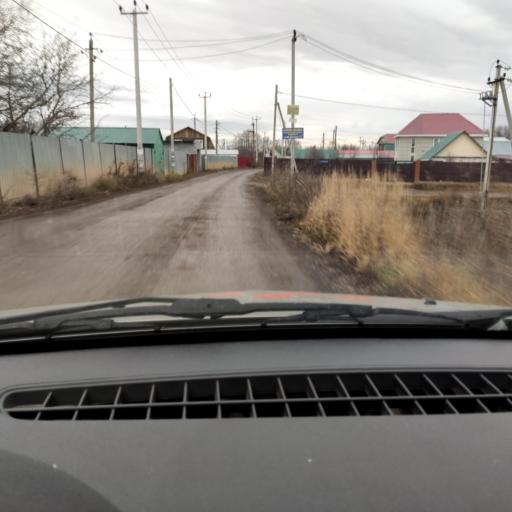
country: RU
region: Bashkortostan
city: Mikhaylovka
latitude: 54.8342
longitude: 55.9462
